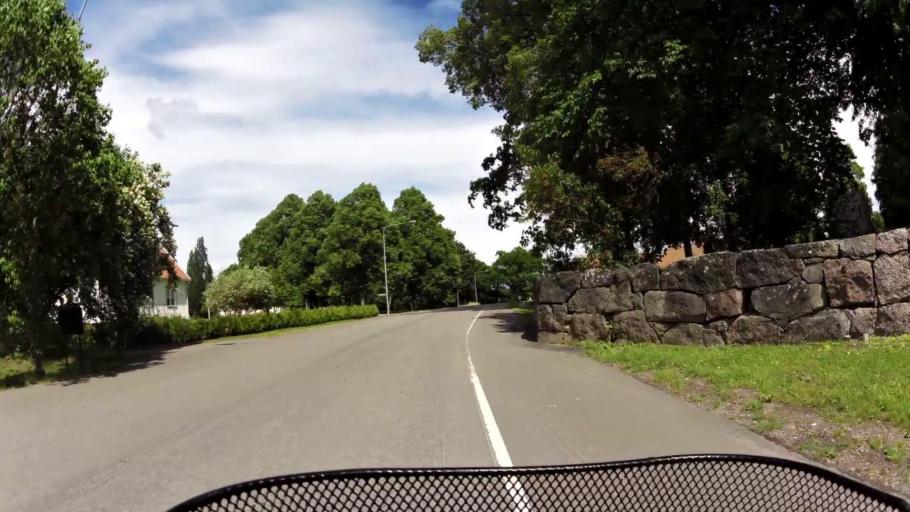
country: SE
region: OEstergoetland
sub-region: Linkopings Kommun
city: Malmslatt
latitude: 58.4170
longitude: 15.5227
